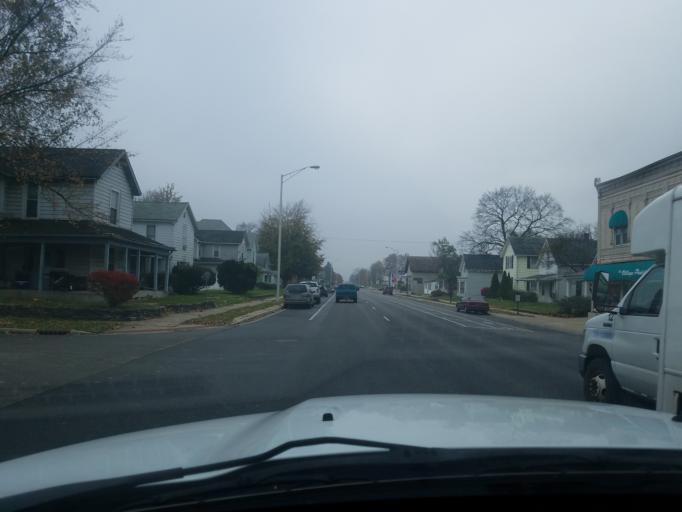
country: US
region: Indiana
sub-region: Cass County
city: Logansport
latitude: 40.7576
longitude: -86.3448
